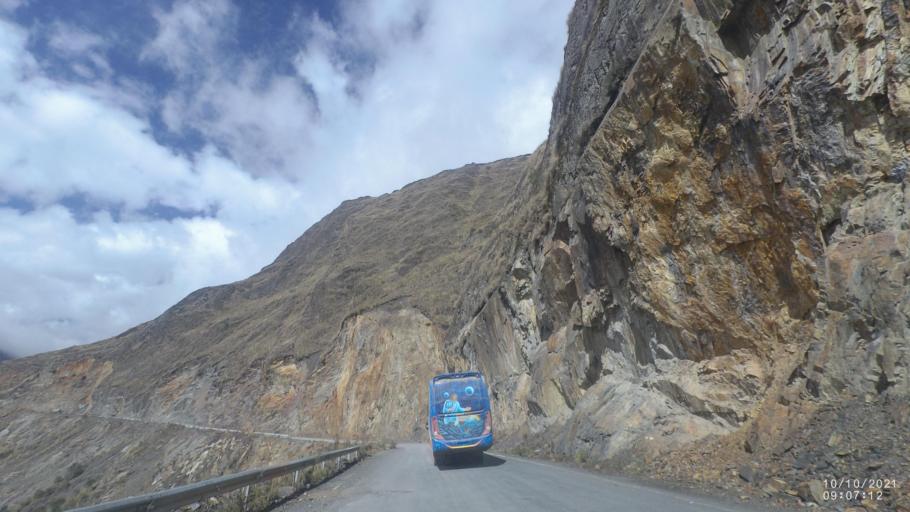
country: BO
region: La Paz
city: Quime
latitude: -17.0086
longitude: -67.2747
